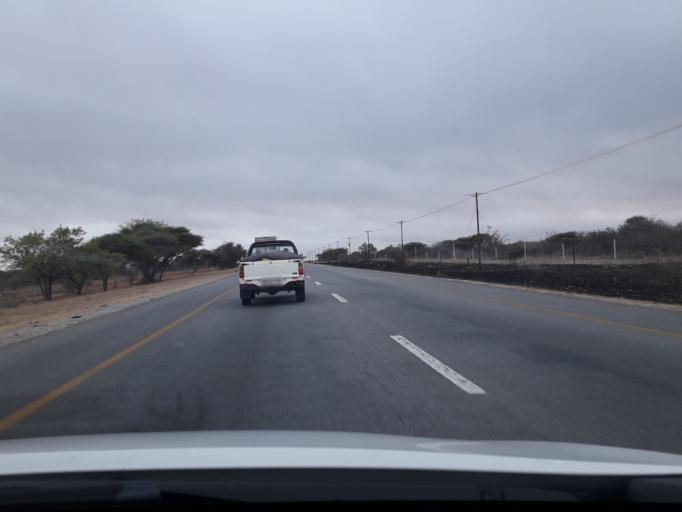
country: ZA
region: Limpopo
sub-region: Capricorn District Municipality
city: Mankoeng
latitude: -23.5887
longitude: 29.6635
